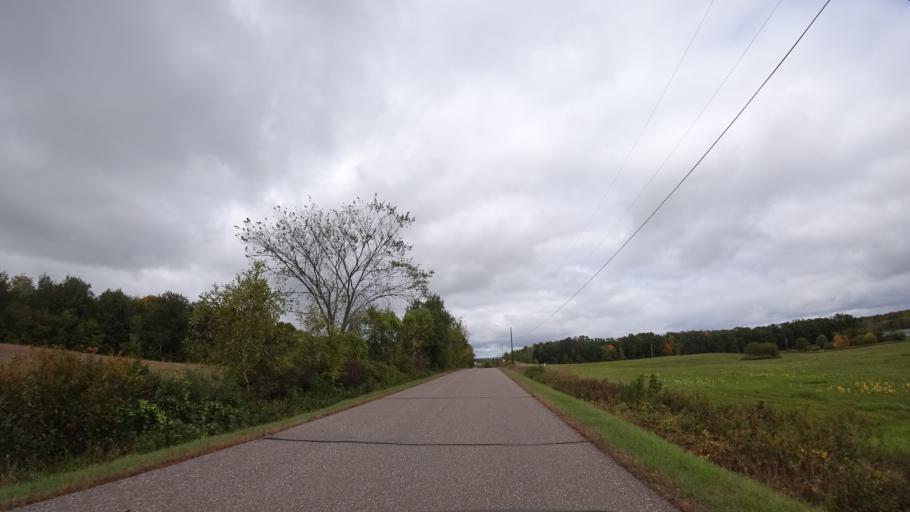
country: US
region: Wisconsin
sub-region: Chippewa County
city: Lake Wissota
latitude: 44.9928
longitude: -91.2867
